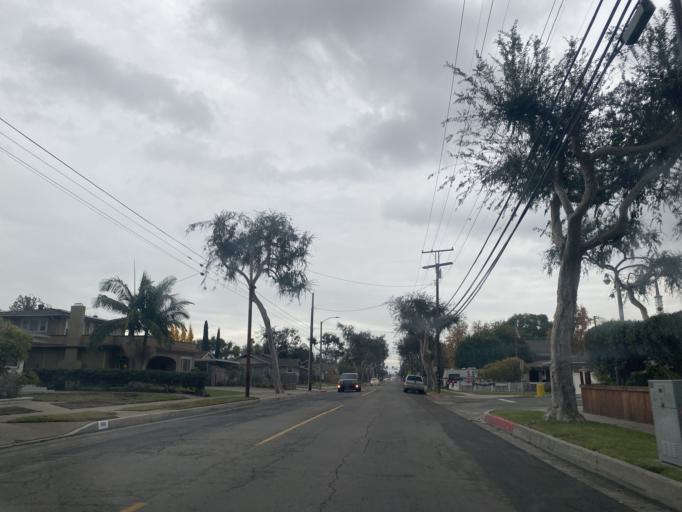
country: US
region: California
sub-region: Orange County
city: Fullerton
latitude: 33.8780
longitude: -117.9071
